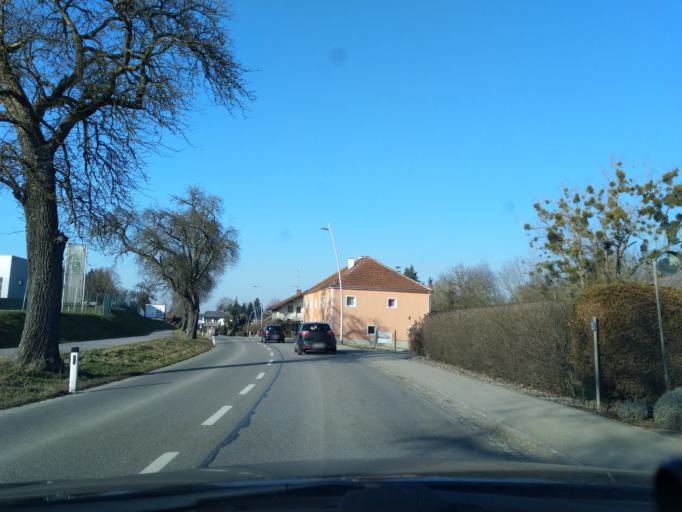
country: AT
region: Upper Austria
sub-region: Politischer Bezirk Ried im Innkreis
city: Ried im Innkreis
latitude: 48.2848
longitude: 13.4433
